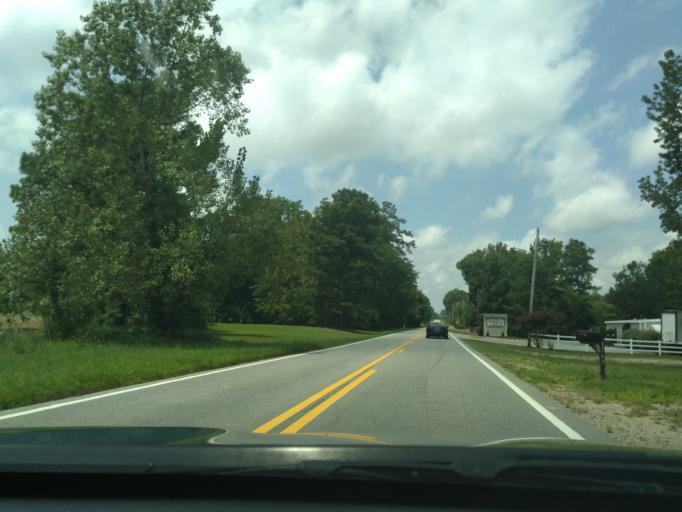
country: US
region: North Carolina
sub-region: Nash County
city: Red Oak
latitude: 36.0019
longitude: -77.8404
